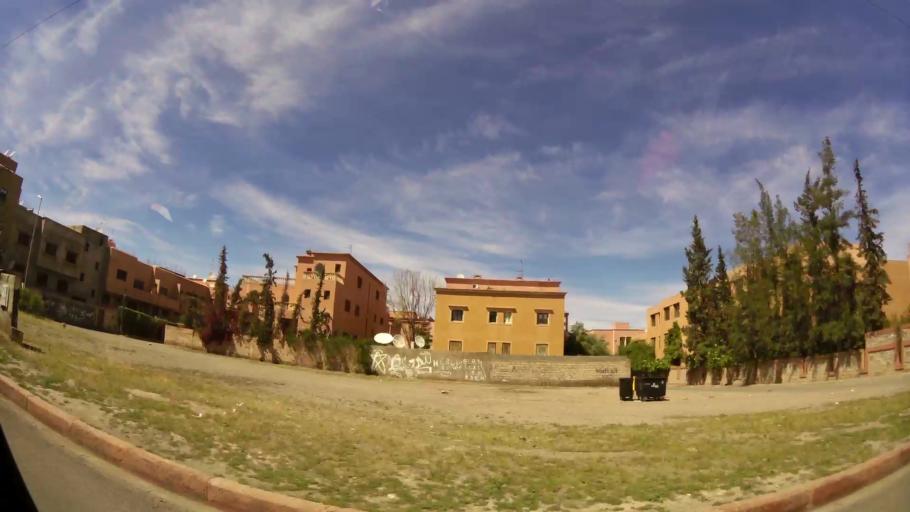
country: MA
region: Marrakech-Tensift-Al Haouz
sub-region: Marrakech
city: Marrakesh
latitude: 31.6600
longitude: -8.0015
